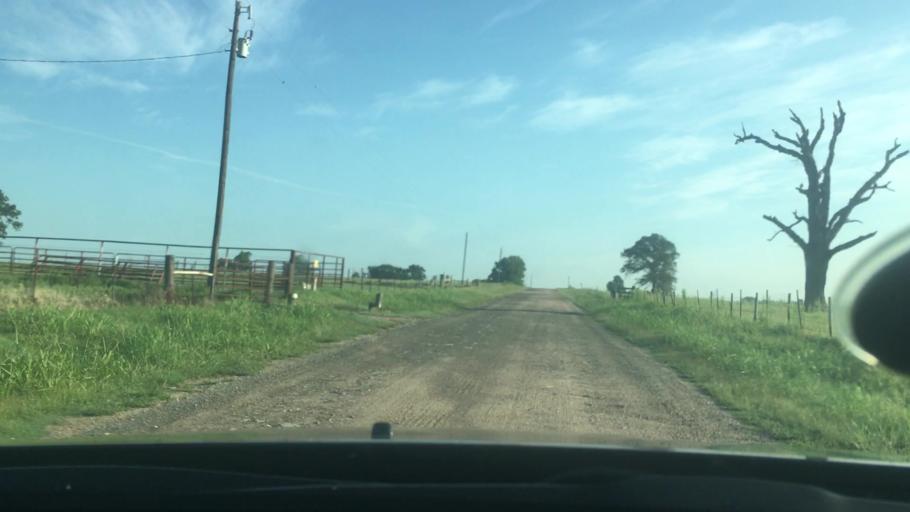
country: US
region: Oklahoma
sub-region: Pontotoc County
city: Ada
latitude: 34.8195
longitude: -96.7748
